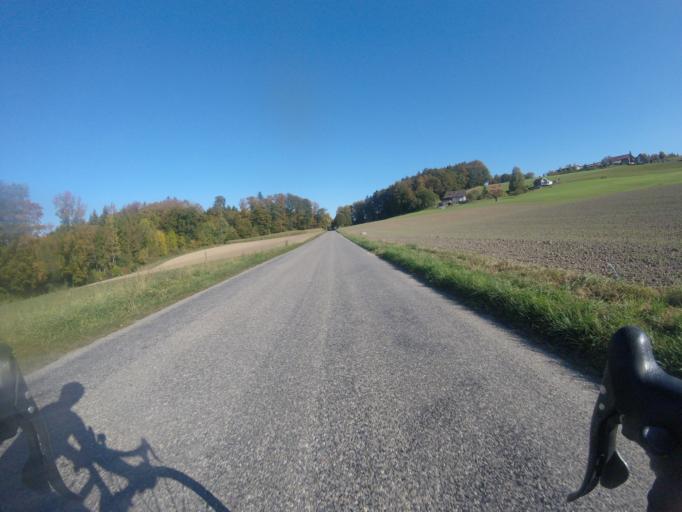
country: CH
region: Bern
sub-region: Seeland District
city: Schupfen
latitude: 47.0399
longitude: 7.3580
